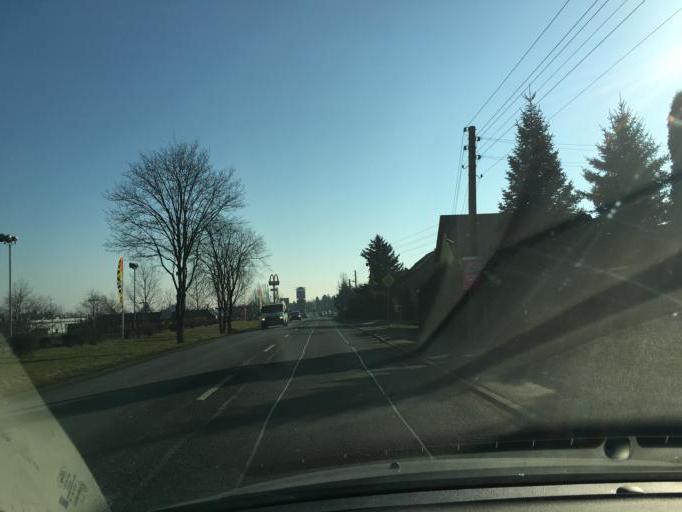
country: DE
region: Saxony
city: Grossposna
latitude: 51.2660
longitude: 12.4956
